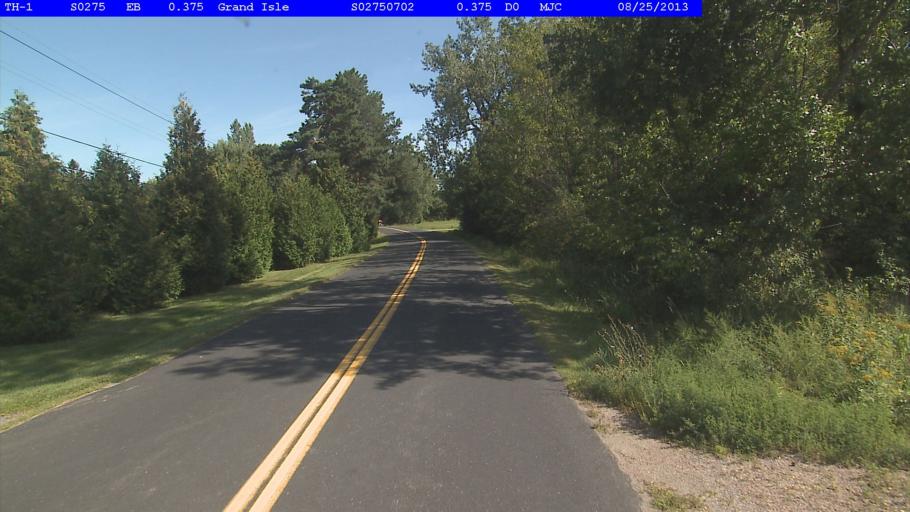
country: US
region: New York
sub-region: Clinton County
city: Cumberland Head
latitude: 44.7061
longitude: -73.3446
